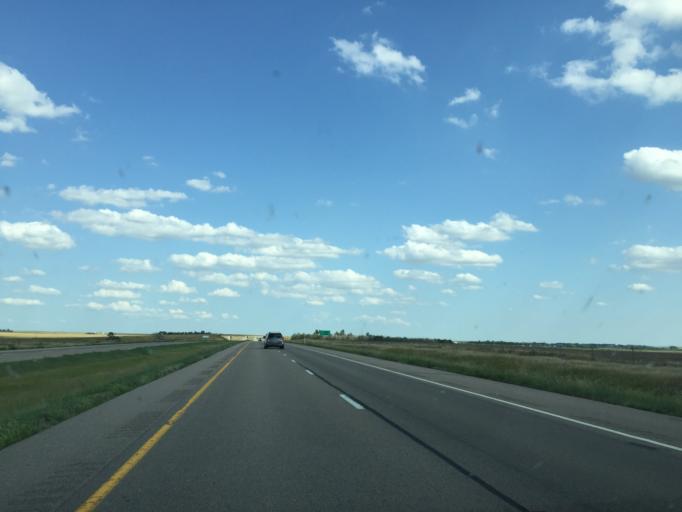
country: US
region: Kansas
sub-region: Gove County
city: Gove
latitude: 39.0527
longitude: -100.2308
